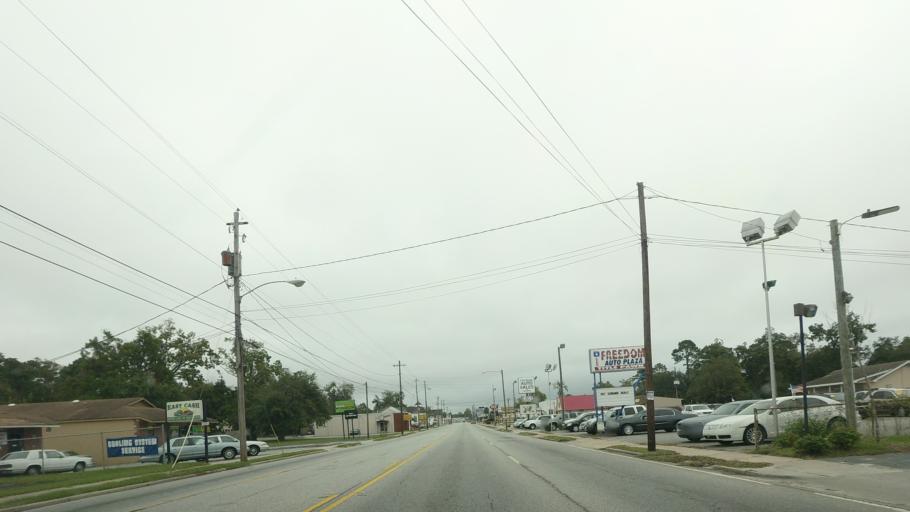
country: US
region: Georgia
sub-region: Lowndes County
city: Valdosta
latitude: 30.8374
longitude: -83.2797
